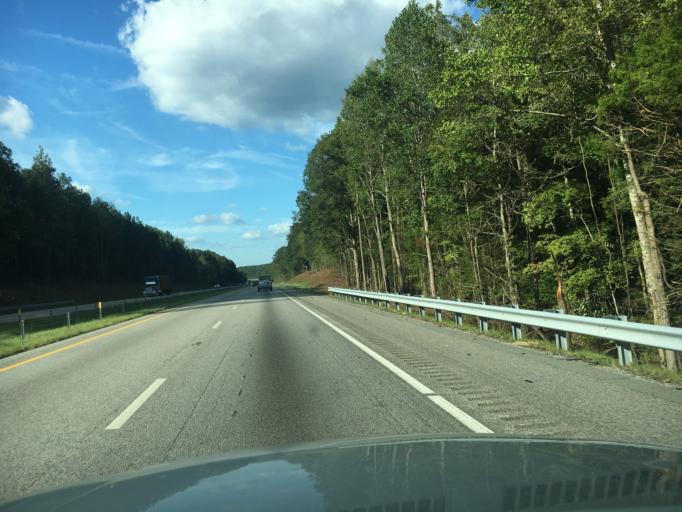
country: US
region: South Carolina
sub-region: Laurens County
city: Clinton
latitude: 34.5866
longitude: -81.8926
